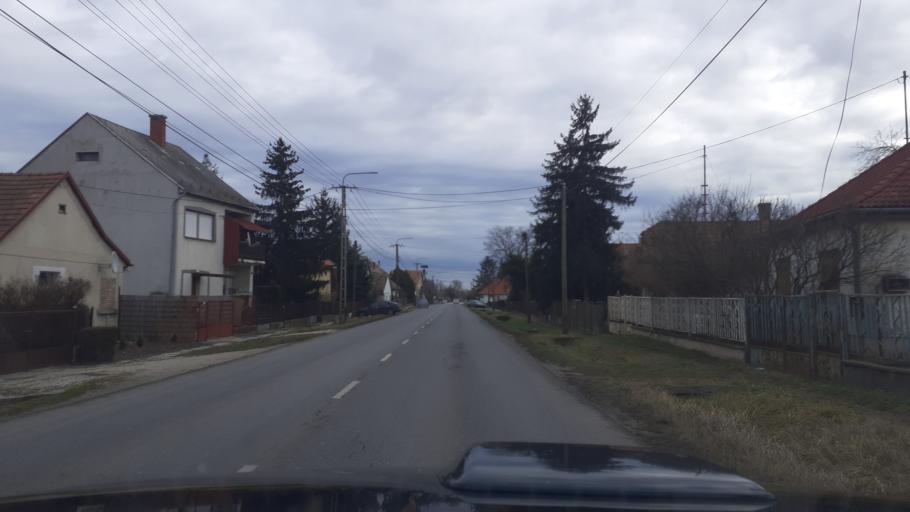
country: HU
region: Fejer
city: Seregelyes
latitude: 47.1182
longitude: 18.5680
